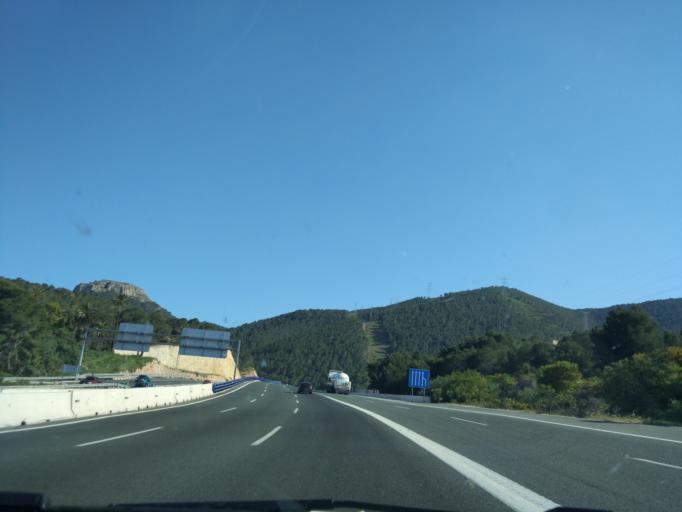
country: ES
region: Murcia
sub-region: Murcia
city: Alcantarilla
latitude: 37.9132
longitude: -1.1650
